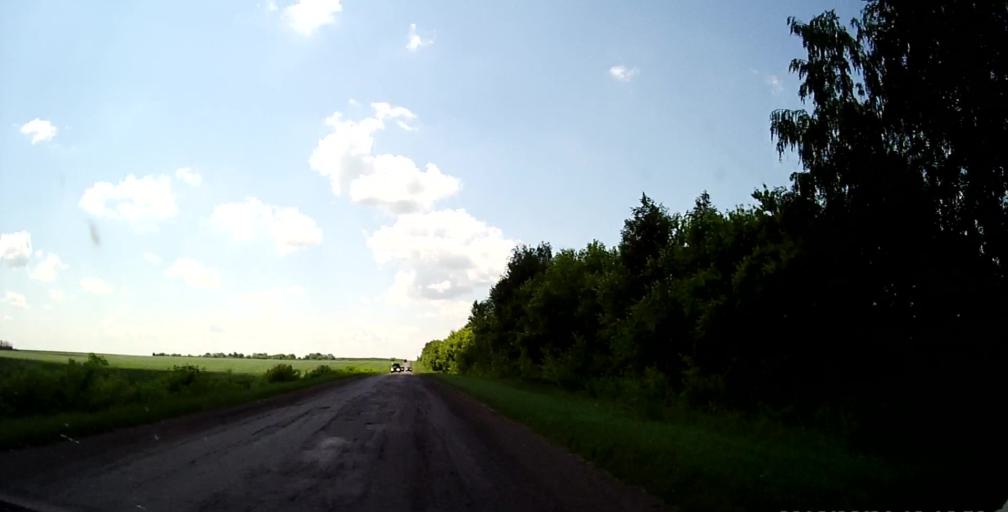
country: RU
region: Lipetsk
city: Chaplygin
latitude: 53.2821
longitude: 39.9612
